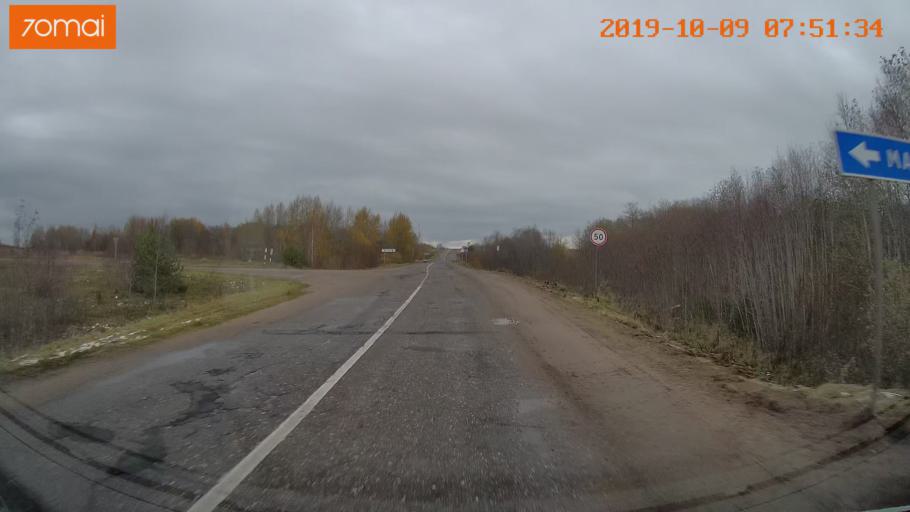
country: RU
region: Jaroslavl
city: Kukoboy
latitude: 58.6841
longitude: 39.8796
